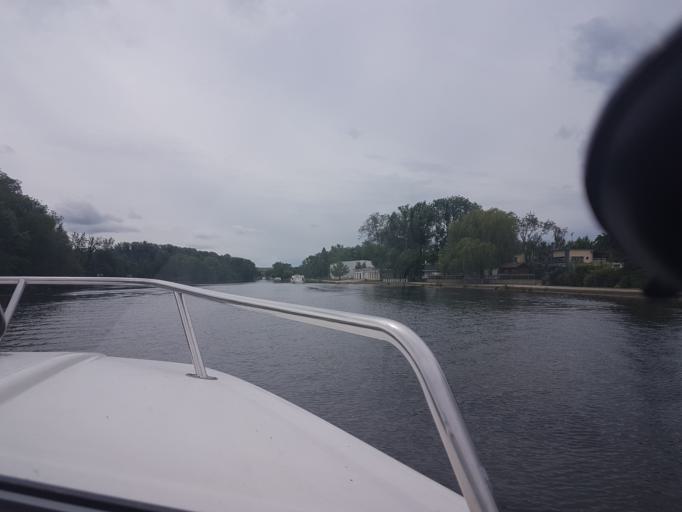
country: FR
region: Bourgogne
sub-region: Departement de l'Yonne
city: Auxerre
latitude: 47.7908
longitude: 3.5878
